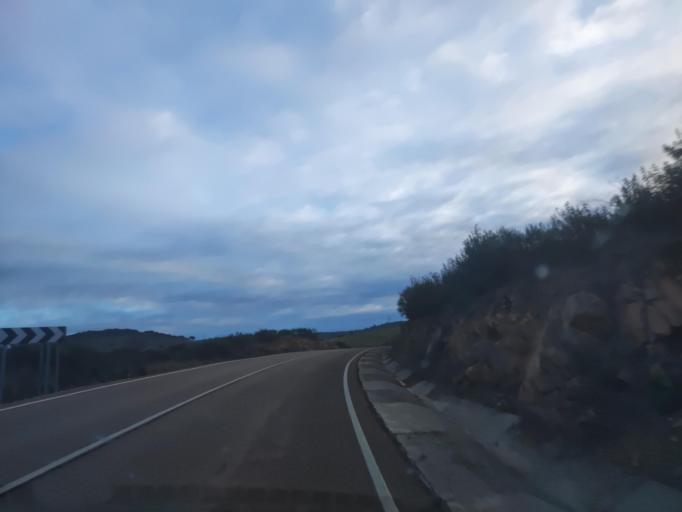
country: ES
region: Castille and Leon
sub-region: Provincia de Salamanca
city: Castillejo de Martin Viejo
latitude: 40.7266
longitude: -6.6384
